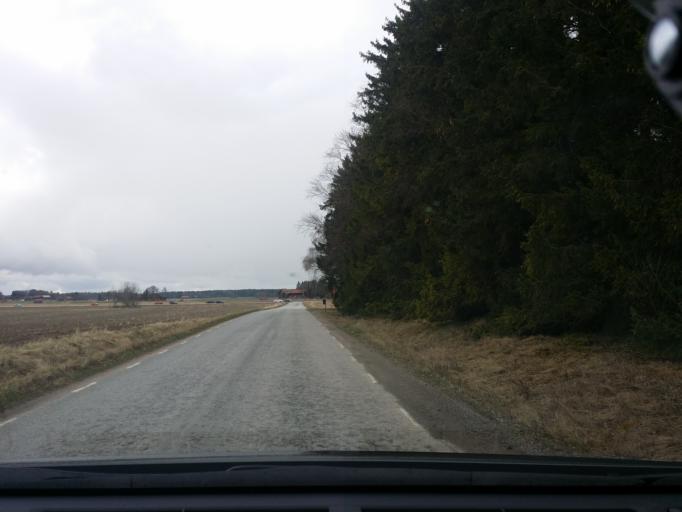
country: SE
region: Uppsala
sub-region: Enkopings Kommun
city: Enkoping
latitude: 59.6798
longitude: 17.0383
